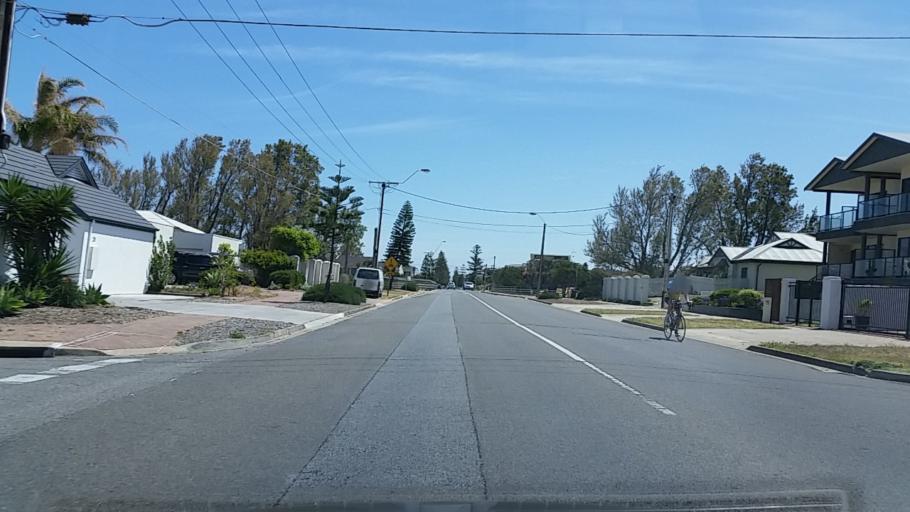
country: AU
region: South Australia
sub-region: Charles Sturt
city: Henley Beach
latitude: -34.9361
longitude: 138.4994
